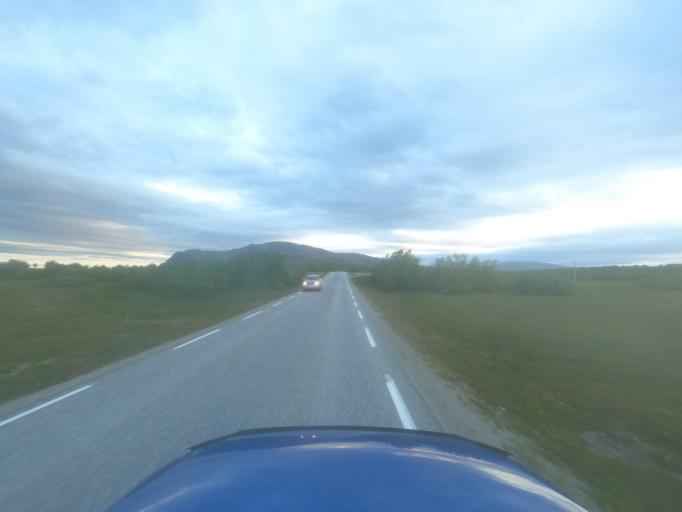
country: NO
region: Finnmark Fylke
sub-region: Porsanger
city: Lakselv
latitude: 70.1638
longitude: 24.9010
